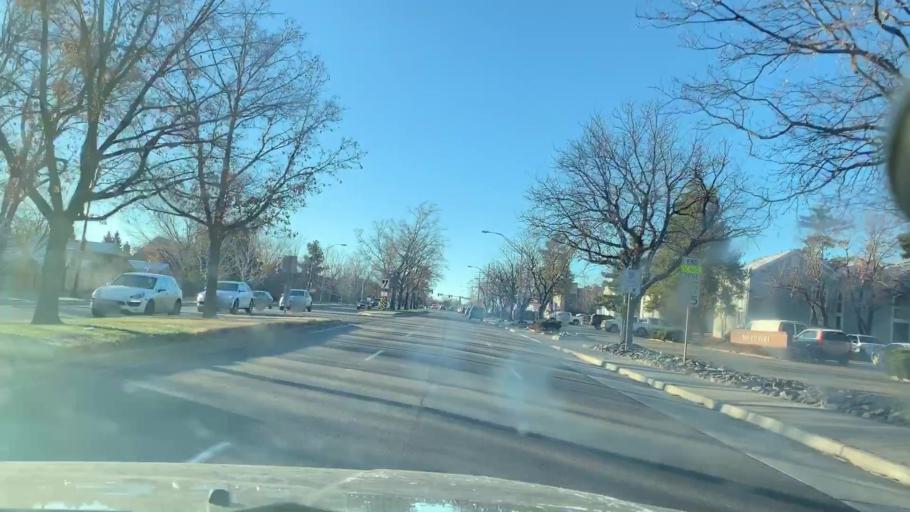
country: US
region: Colorado
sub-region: Arapahoe County
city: Cherry Hills Village
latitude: 39.6558
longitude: -104.9130
